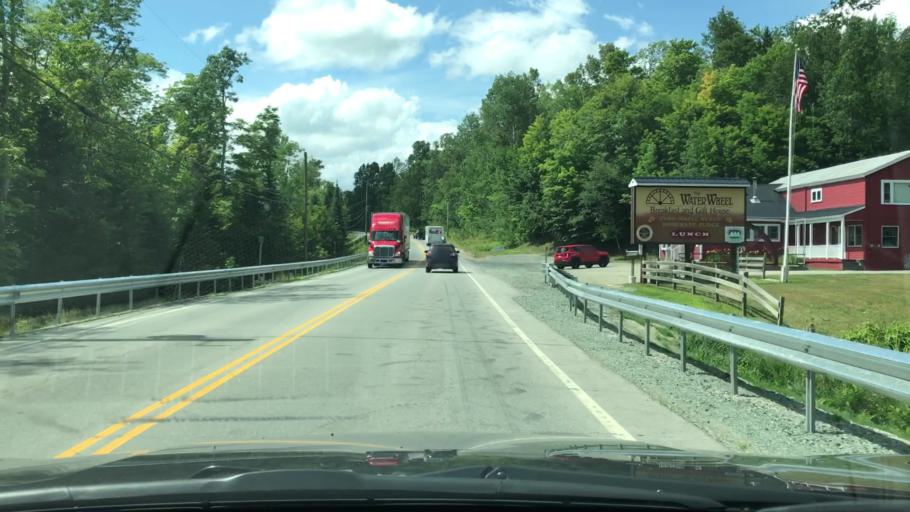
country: US
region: New Hampshire
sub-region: Coos County
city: Jefferson
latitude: 44.3643
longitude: -71.3913
